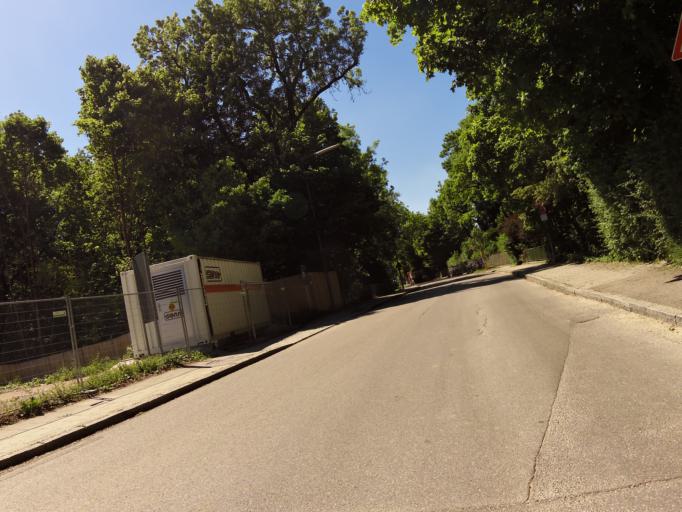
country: DE
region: Bavaria
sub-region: Upper Bavaria
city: Unterfoehring
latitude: 48.1906
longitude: 11.6268
